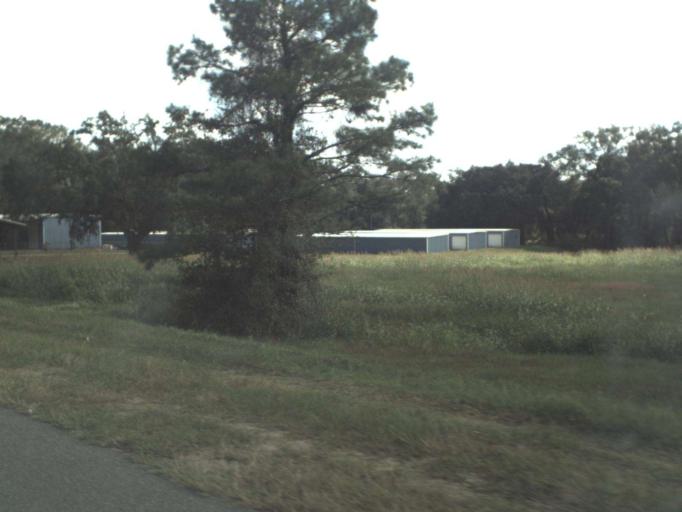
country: US
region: Florida
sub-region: Jackson County
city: Sneads
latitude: 30.7107
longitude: -84.9407
